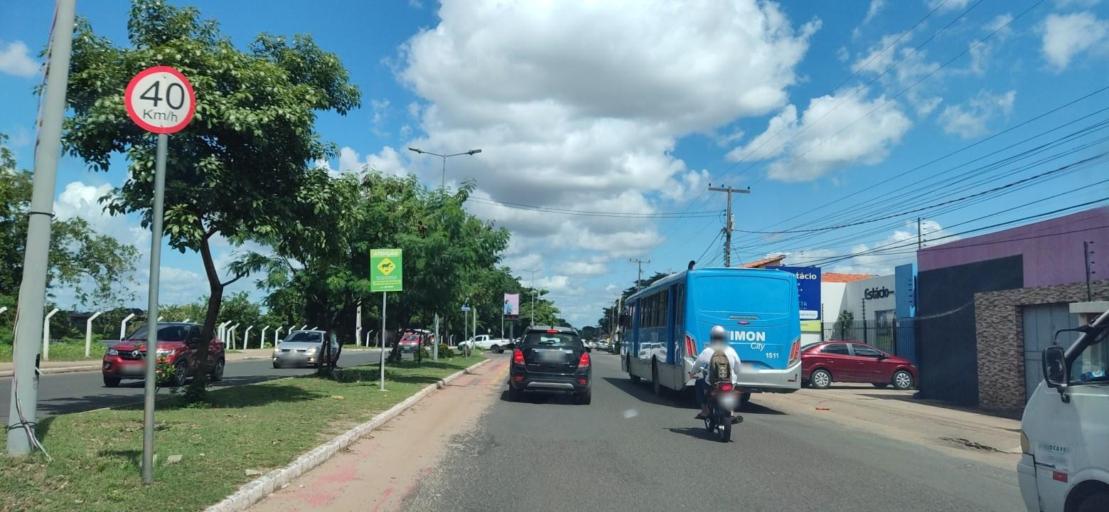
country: BR
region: Maranhao
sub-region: Timon
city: Timon
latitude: -5.0929
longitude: -42.8224
